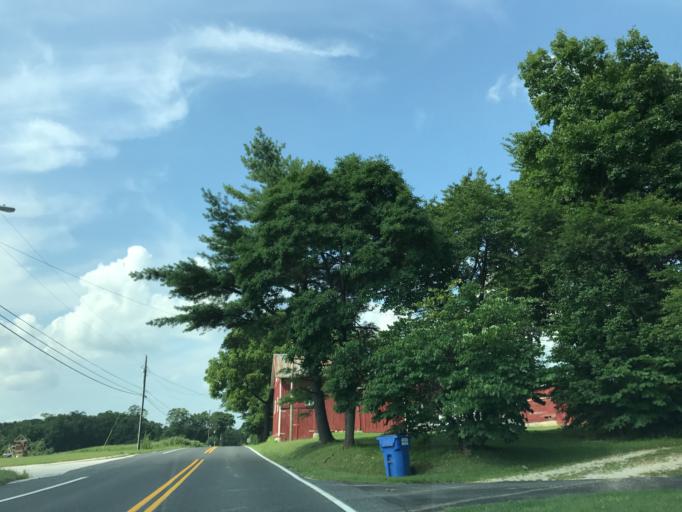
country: US
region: Pennsylvania
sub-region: York County
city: Pennville
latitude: 39.7404
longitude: -77.0012
